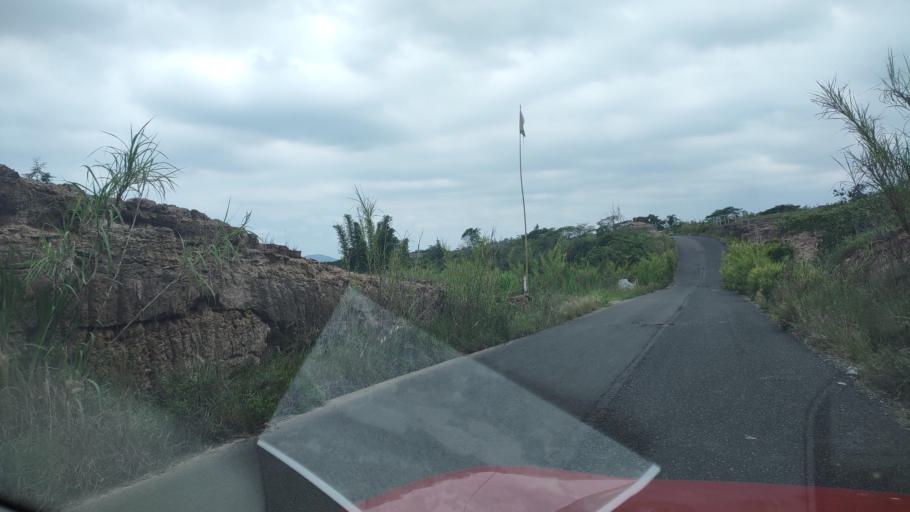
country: MX
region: Veracruz
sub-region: Emiliano Zapata
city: Dos Rios
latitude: 19.4843
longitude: -96.8269
